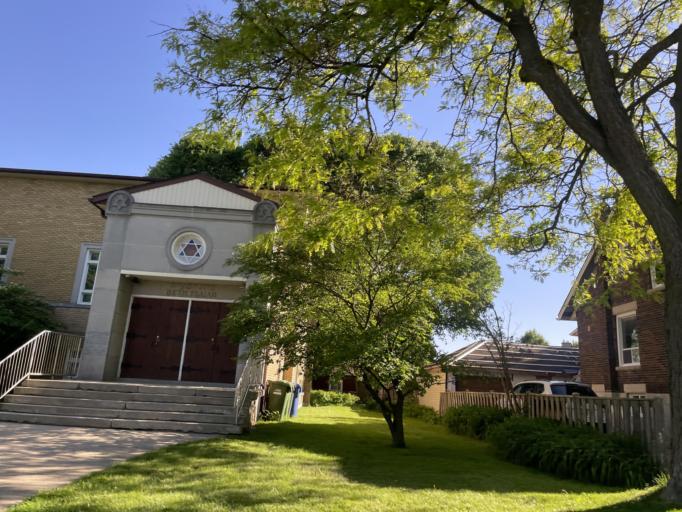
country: CA
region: Ontario
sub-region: Wellington County
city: Guelph
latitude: 43.5397
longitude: -80.2469
